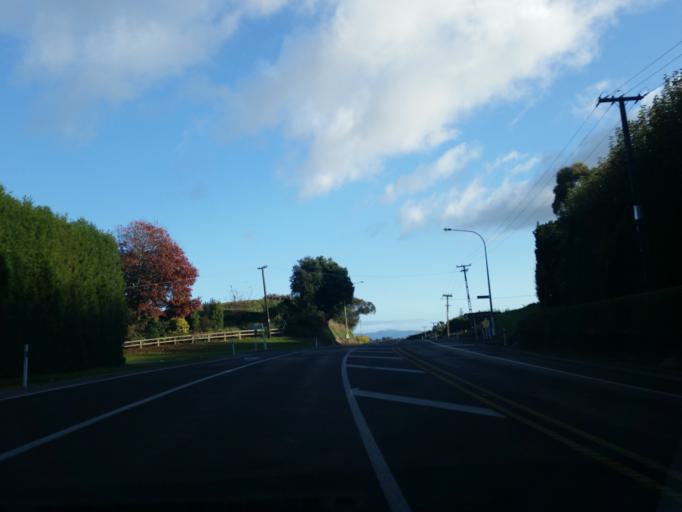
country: NZ
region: Bay of Plenty
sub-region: Tauranga City
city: Tauranga
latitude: -37.6960
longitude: 176.0506
